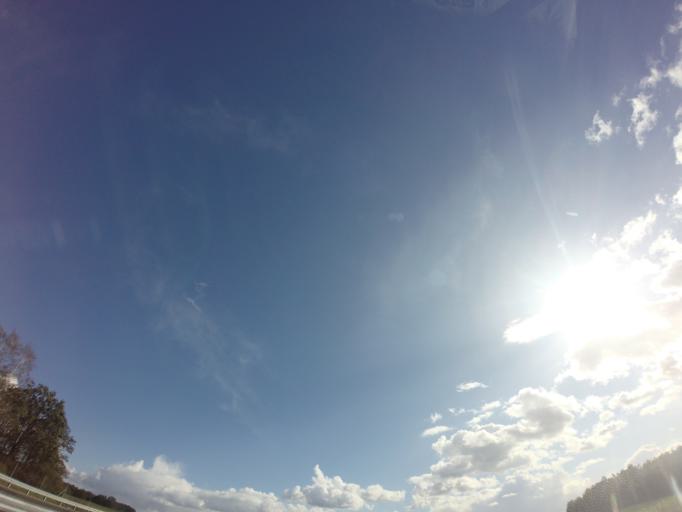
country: PL
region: Lubusz
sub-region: Powiat nowosolski
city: Nowe Miasteczko
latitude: 51.7036
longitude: 15.7527
